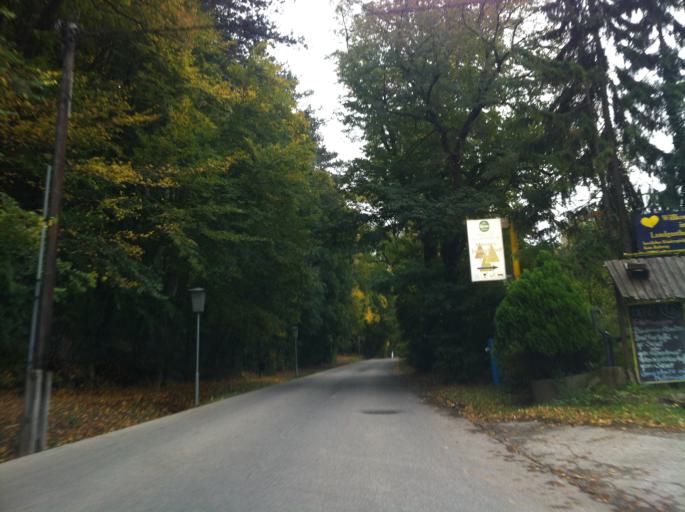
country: AT
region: Lower Austria
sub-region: Politischer Bezirk Wien-Umgebung
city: Purkersdorf
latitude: 48.1985
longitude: 16.1672
